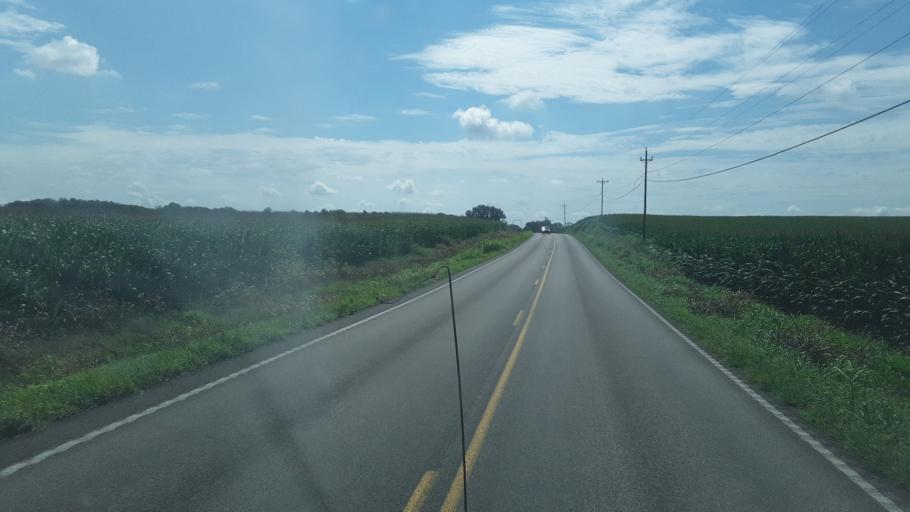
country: US
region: Kentucky
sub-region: Christian County
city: Oak Grove
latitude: 36.7718
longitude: -87.3398
